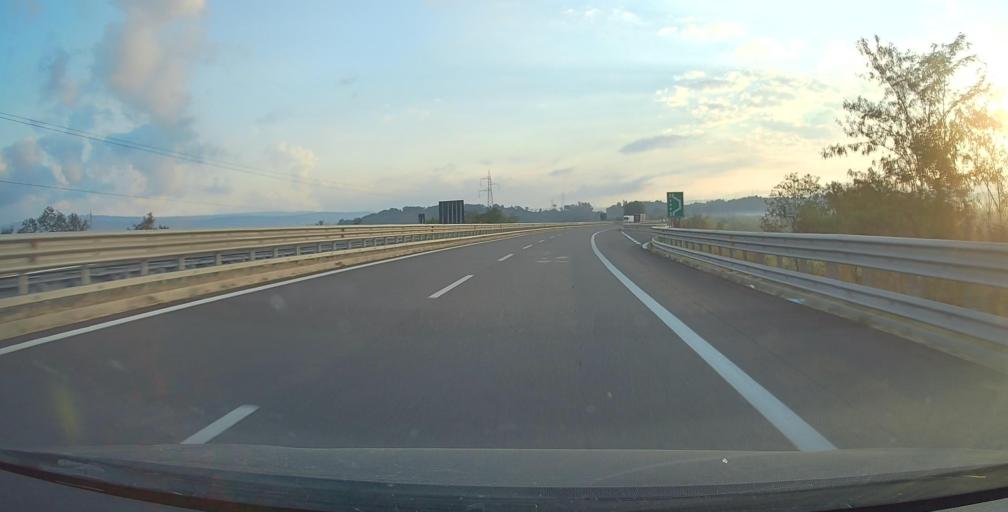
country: IT
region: Calabria
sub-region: Provincia di Reggio Calabria
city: Rosarno
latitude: 38.4849
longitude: 16.0034
